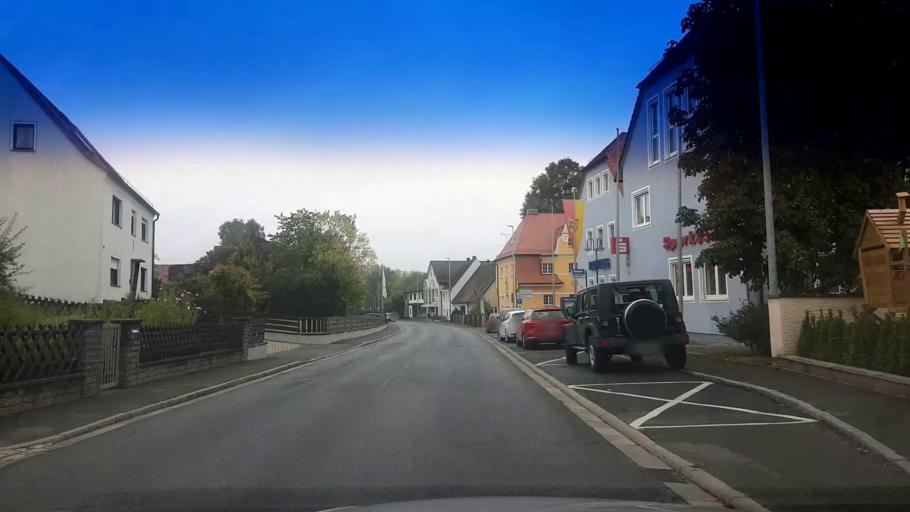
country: DE
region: Bavaria
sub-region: Upper Franconia
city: Heroldsbach
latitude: 49.6925
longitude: 10.9995
